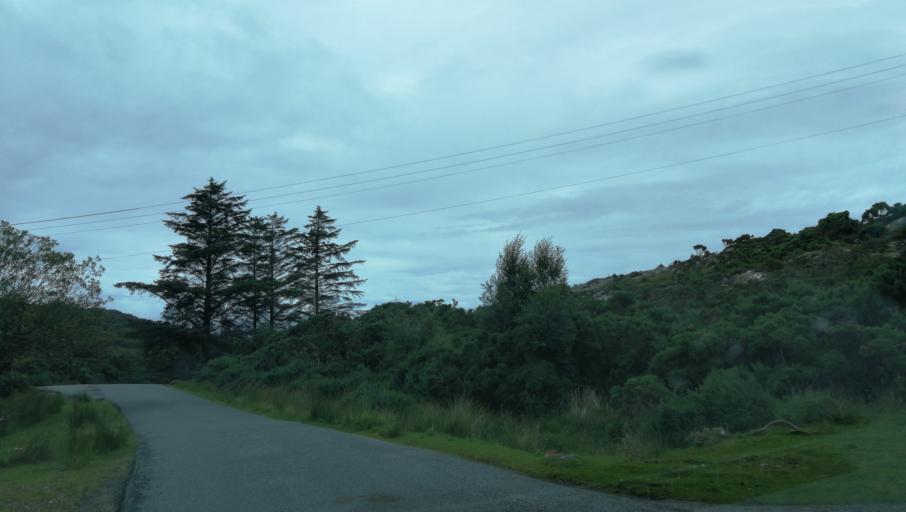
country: GB
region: Scotland
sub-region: Highland
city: Ullapool
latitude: 58.1341
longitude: -5.2613
